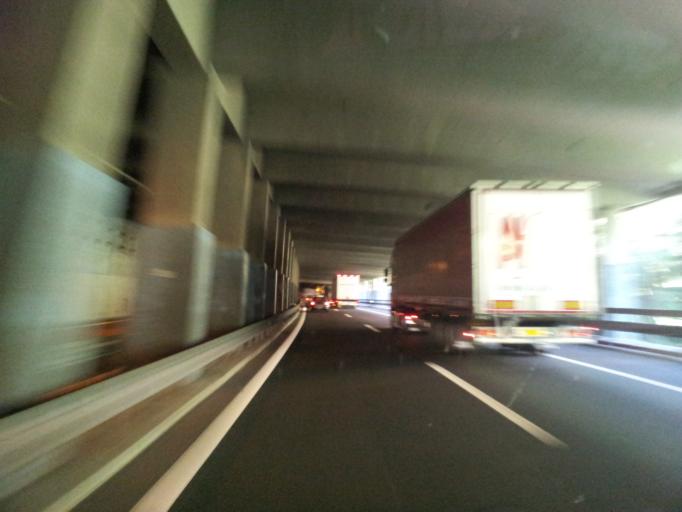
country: CH
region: Uri
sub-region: Uri
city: Andermatt
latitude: 46.7166
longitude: 8.6138
